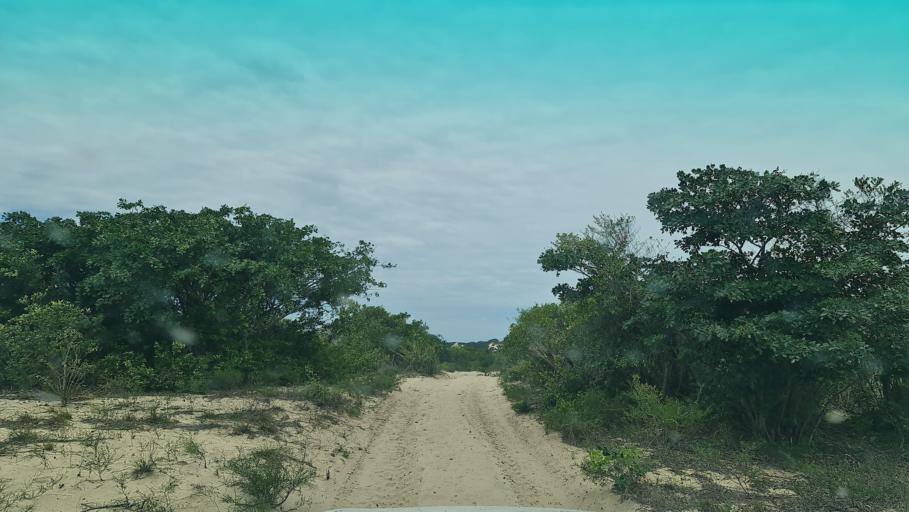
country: MZ
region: Maputo
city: Manhica
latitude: -25.6387
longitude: 32.7763
